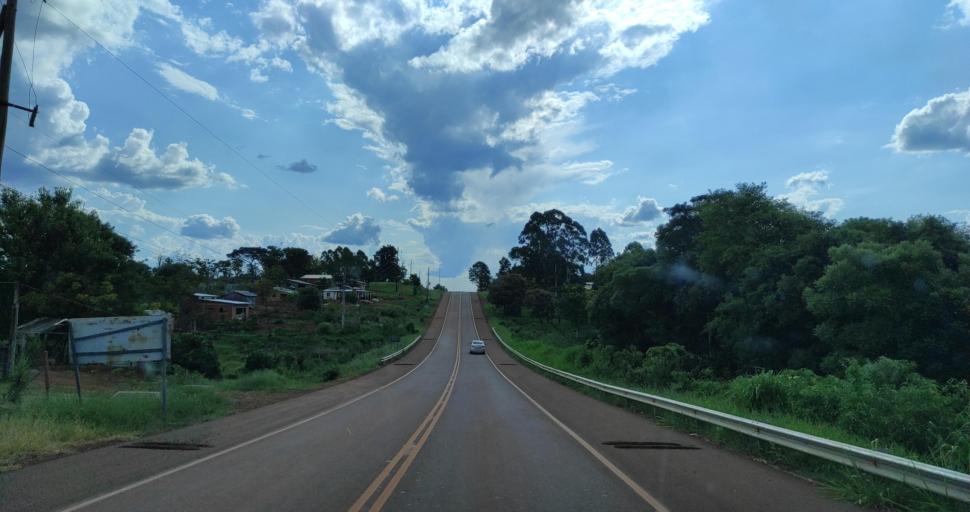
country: AR
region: Misiones
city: Bernardo de Irigoyen
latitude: -26.2929
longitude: -53.7693
